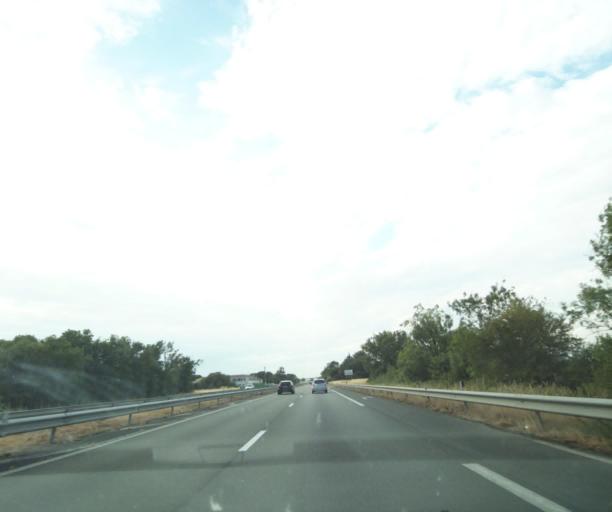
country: FR
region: Poitou-Charentes
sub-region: Departement de la Charente-Maritime
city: Chatelaillon-Plage
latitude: 46.0557
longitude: -1.0559
